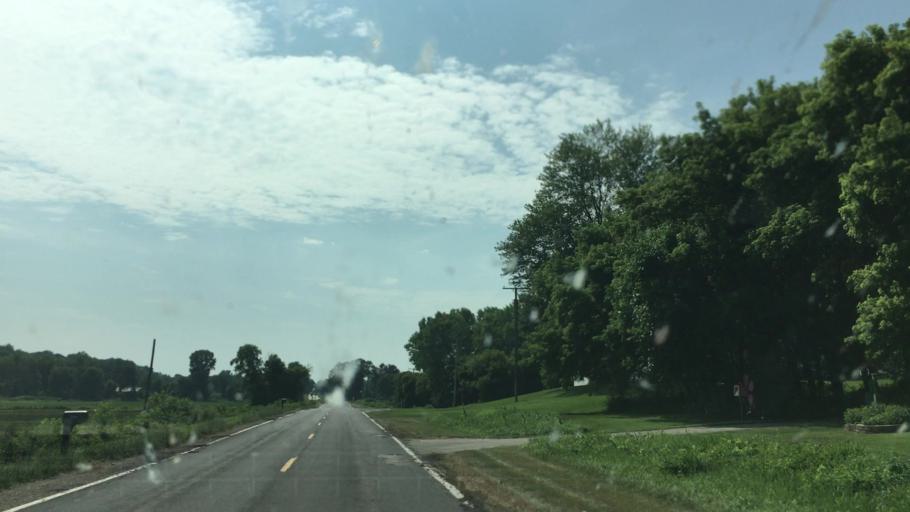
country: US
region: Michigan
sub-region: Kent County
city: Byron Center
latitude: 42.7829
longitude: -85.7748
